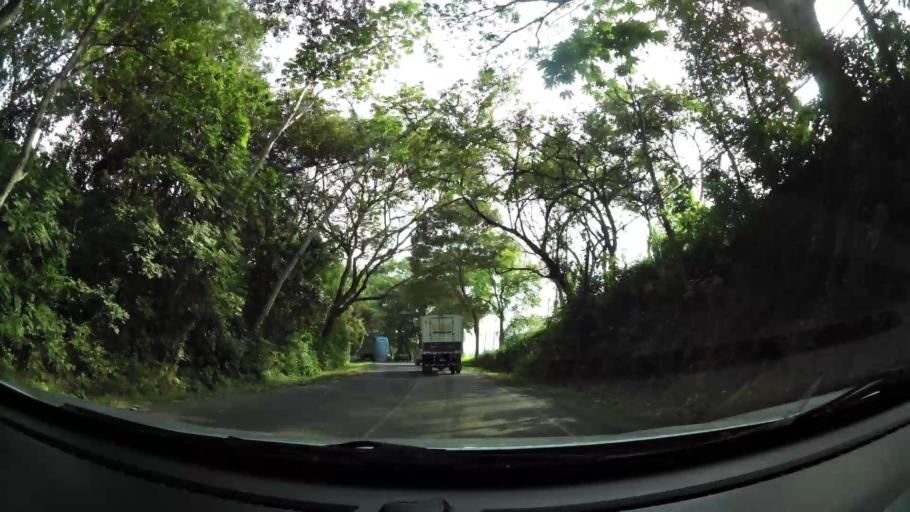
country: CR
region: Guanacaste
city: Juntas
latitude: 10.1867
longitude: -84.9460
